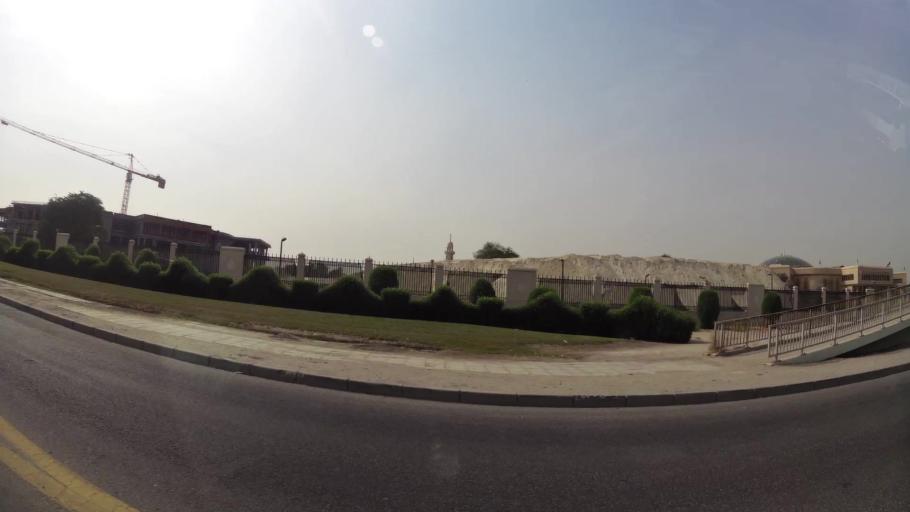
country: KW
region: Al Asimah
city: Ar Rabiyah
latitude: 29.2942
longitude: 47.9466
